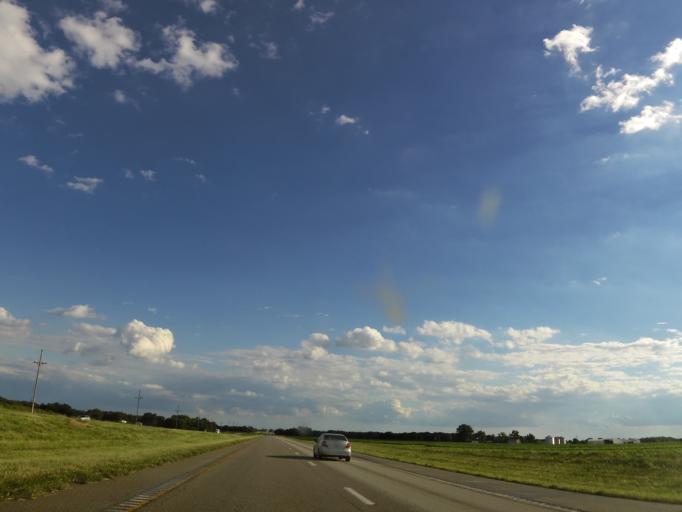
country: US
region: Missouri
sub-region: Lincoln County
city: Troy
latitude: 39.1050
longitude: -90.9629
